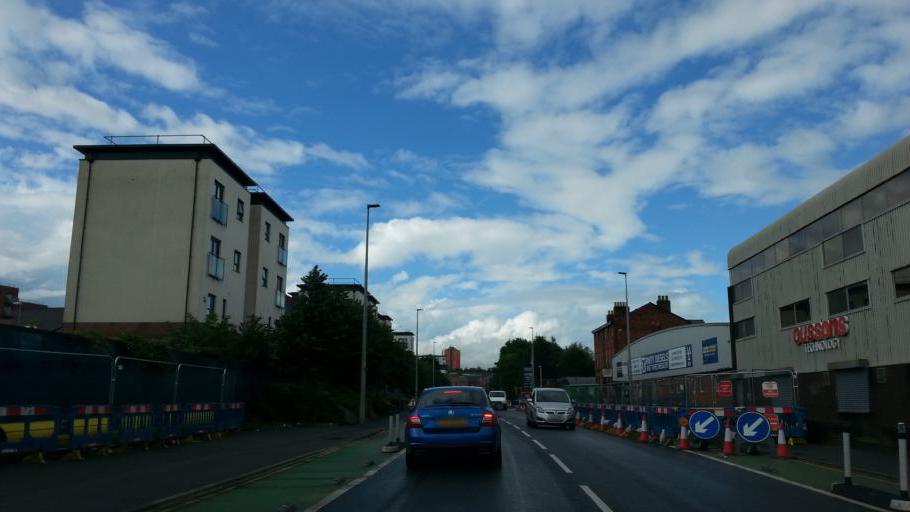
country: GB
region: England
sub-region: Manchester
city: Cheetham Hill
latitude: 53.4947
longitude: -2.2593
